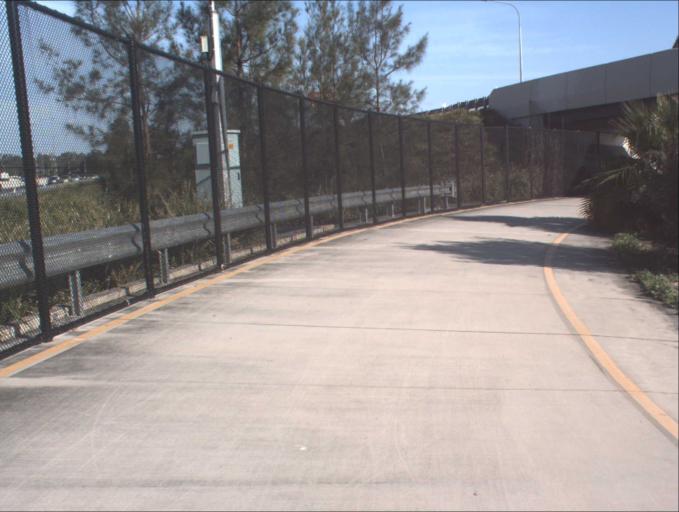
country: AU
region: Queensland
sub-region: Logan
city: Slacks Creek
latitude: -27.6443
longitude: 153.1459
